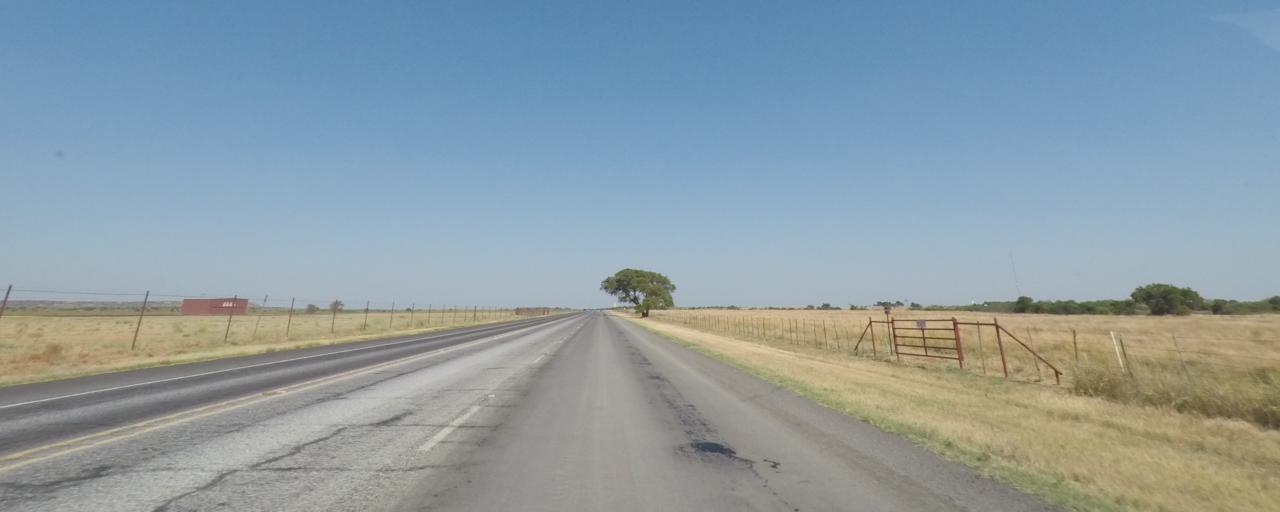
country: US
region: Texas
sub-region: King County
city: Guthrie
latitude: 33.6329
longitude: -100.3520
